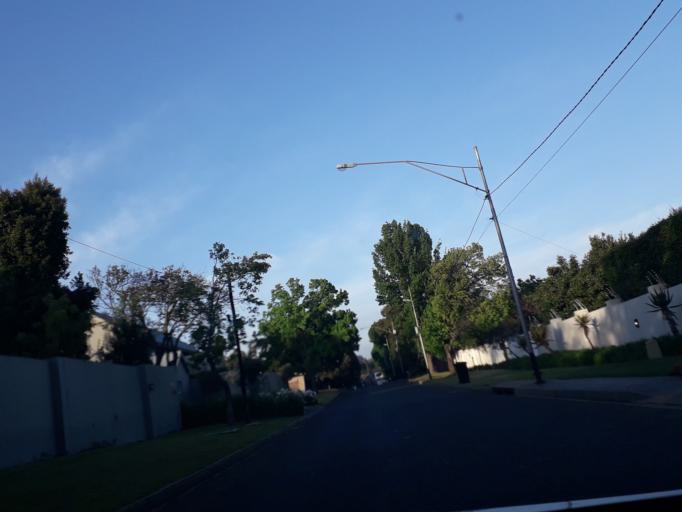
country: ZA
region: Gauteng
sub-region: City of Johannesburg Metropolitan Municipality
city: Johannesburg
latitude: -26.1348
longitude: 28.0821
